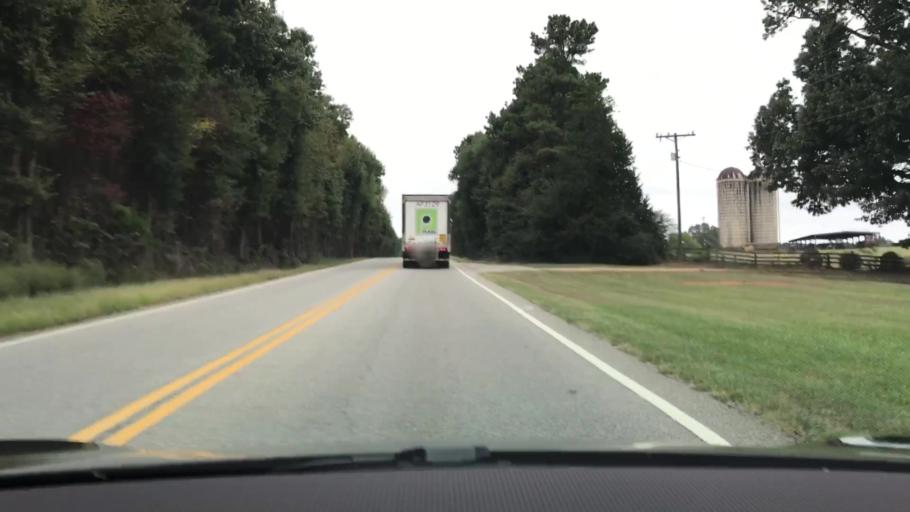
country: US
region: Georgia
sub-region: Greene County
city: Greensboro
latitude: 33.6510
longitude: -83.2355
